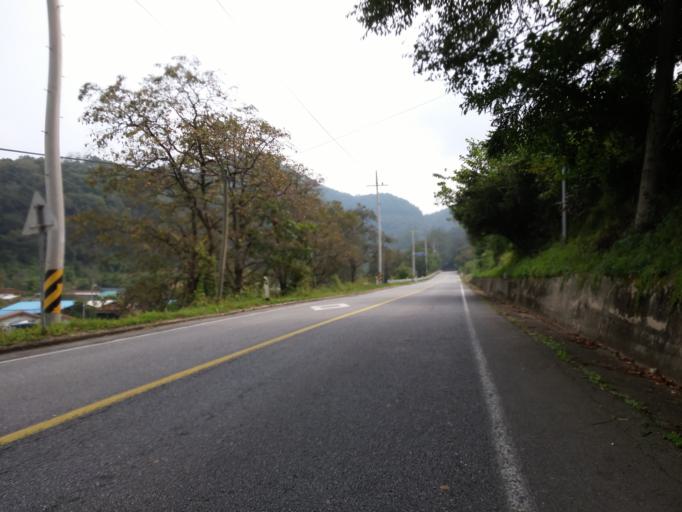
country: KR
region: Chungcheongbuk-do
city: Okcheon
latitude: 36.3925
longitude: 127.6716
